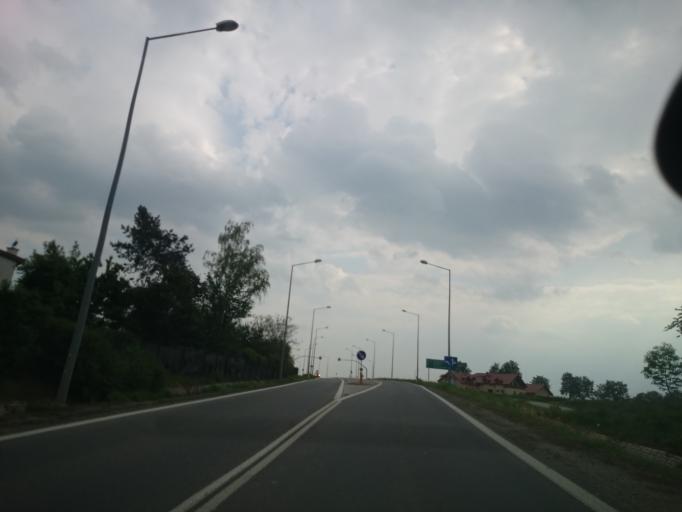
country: PL
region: Lower Silesian Voivodeship
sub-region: Powiat dzierzoniowski
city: Niemcza
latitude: 50.7233
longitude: 16.8254
